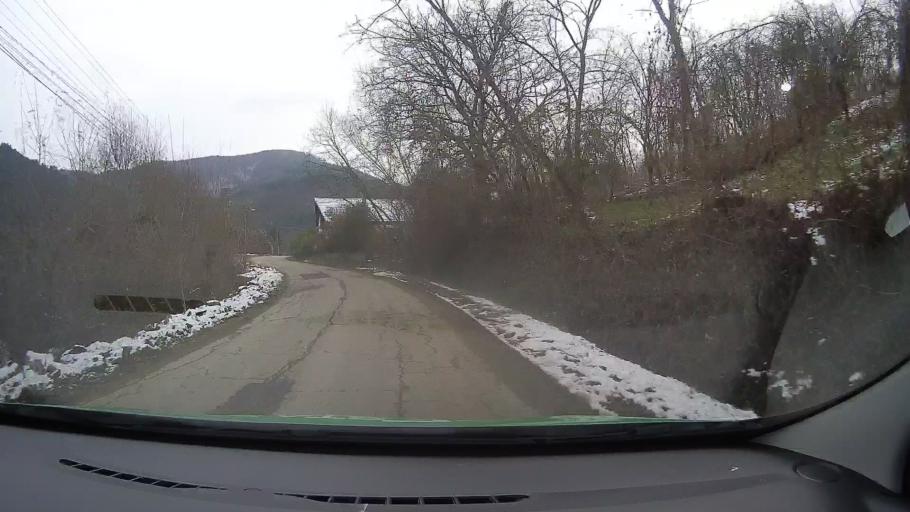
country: RO
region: Hunedoara
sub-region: Comuna Geoagiu
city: Geoagiu
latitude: 45.9760
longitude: 23.1693
